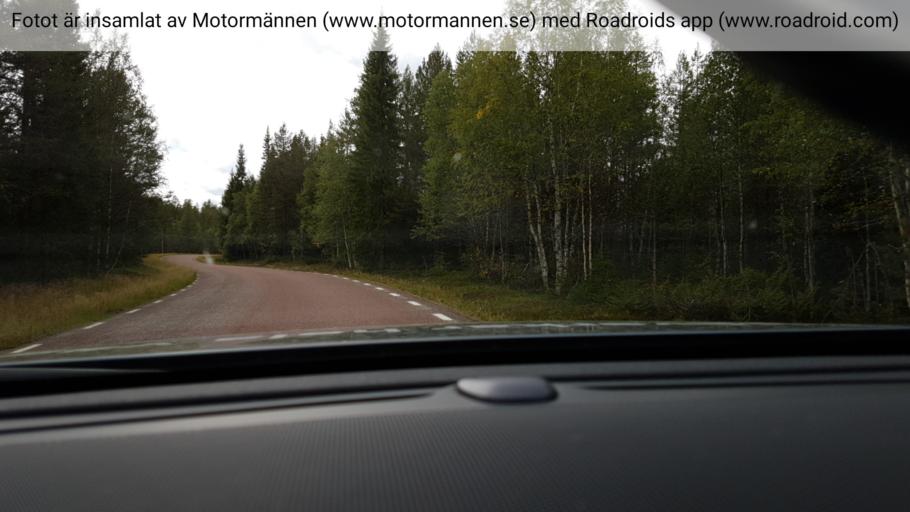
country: NO
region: Hedmark
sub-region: Trysil
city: Innbygda
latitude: 61.6938
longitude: 12.6155
